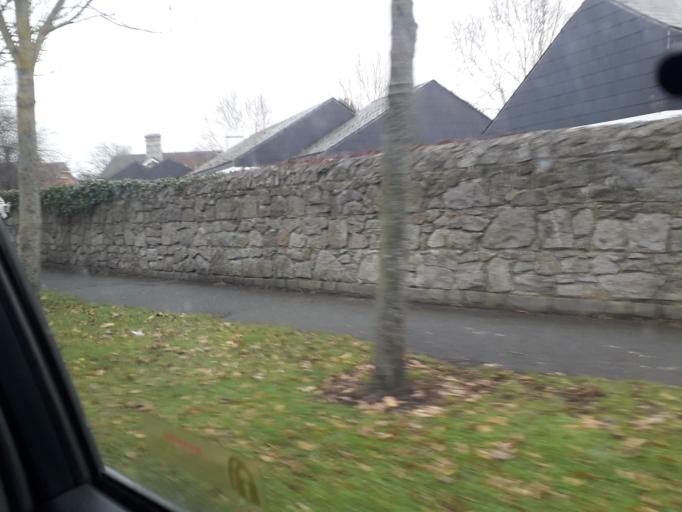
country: IE
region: Leinster
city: Sandymount
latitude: 53.3285
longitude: -6.2144
